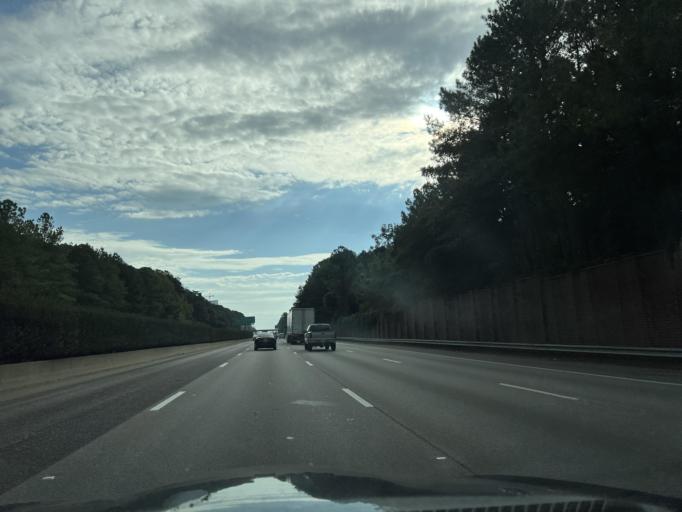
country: US
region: North Carolina
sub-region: Wake County
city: West Raleigh
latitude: 35.8358
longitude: -78.6553
